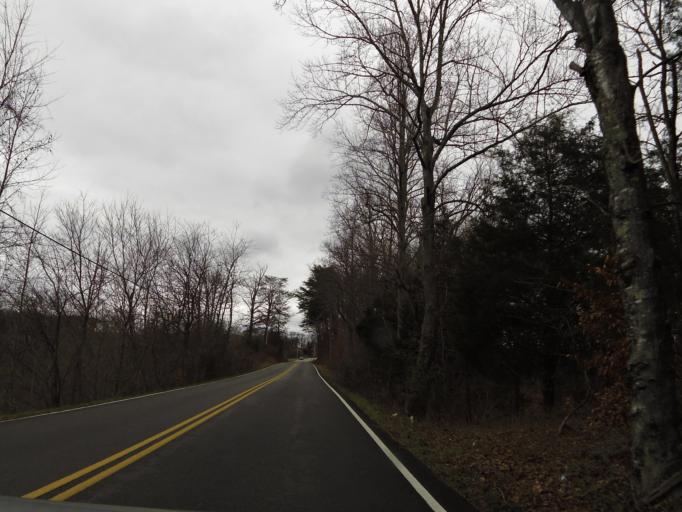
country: US
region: Tennessee
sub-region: Jefferson County
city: New Market
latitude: 36.1624
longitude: -83.6131
